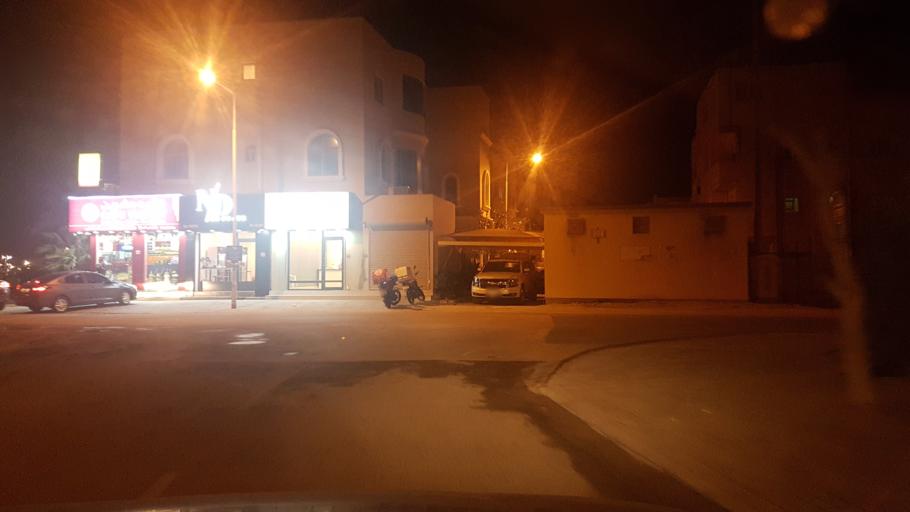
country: BH
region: Muharraq
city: Al Hadd
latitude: 26.2647
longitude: 50.6545
